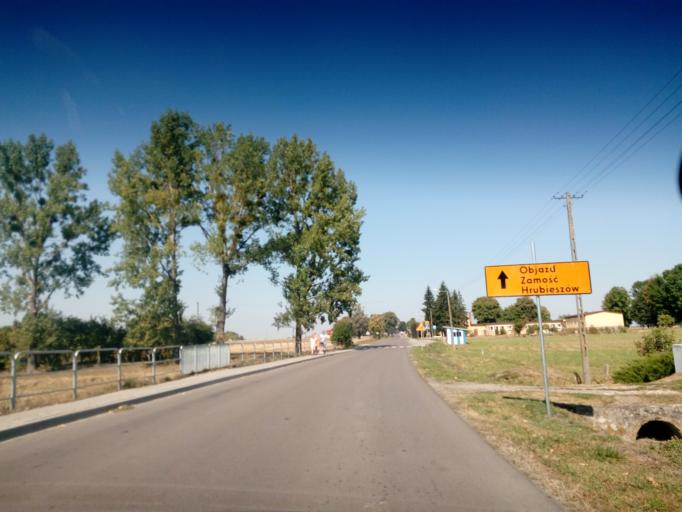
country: PL
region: Lublin Voivodeship
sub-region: Powiat hrubieszowski
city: Mircze
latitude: 50.7288
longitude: 23.9471
